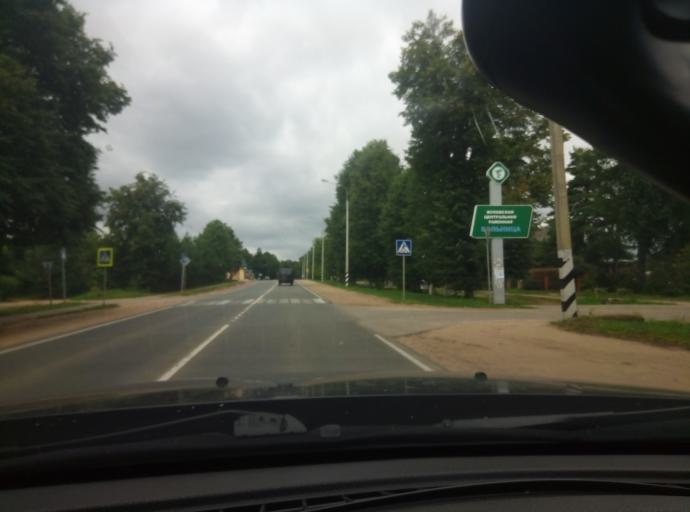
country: RU
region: Kaluga
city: Zhukovo
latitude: 55.0359
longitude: 36.7401
